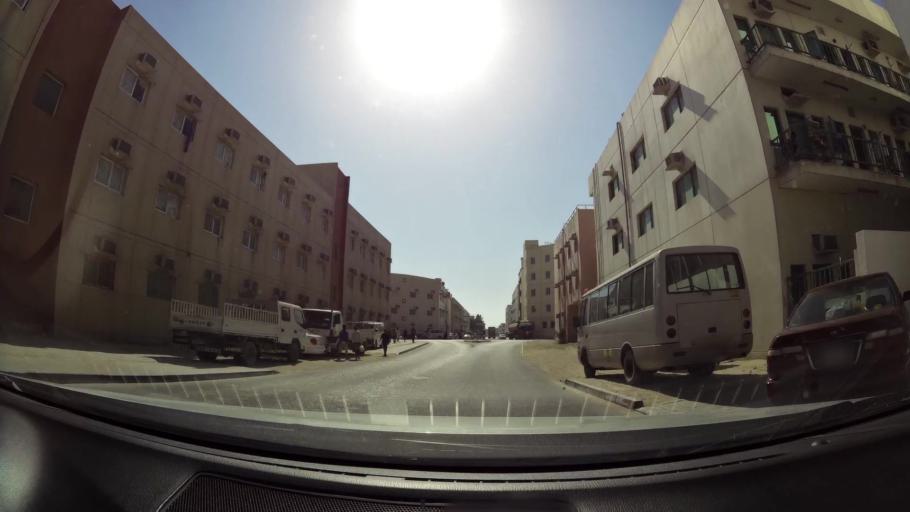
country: AE
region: Dubai
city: Dubai
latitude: 25.0093
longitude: 55.1099
